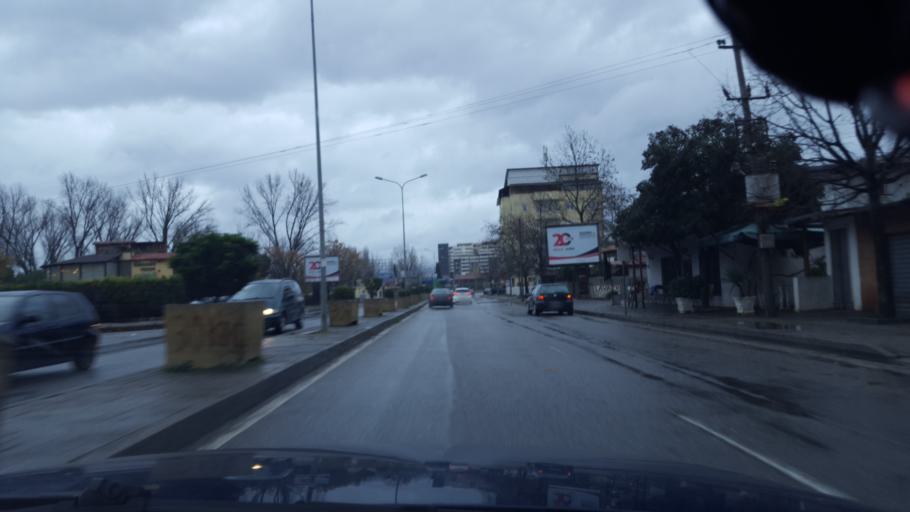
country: AL
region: Shkoder
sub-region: Rrethi i Shkodres
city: Shkoder
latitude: 42.0499
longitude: 19.4935
